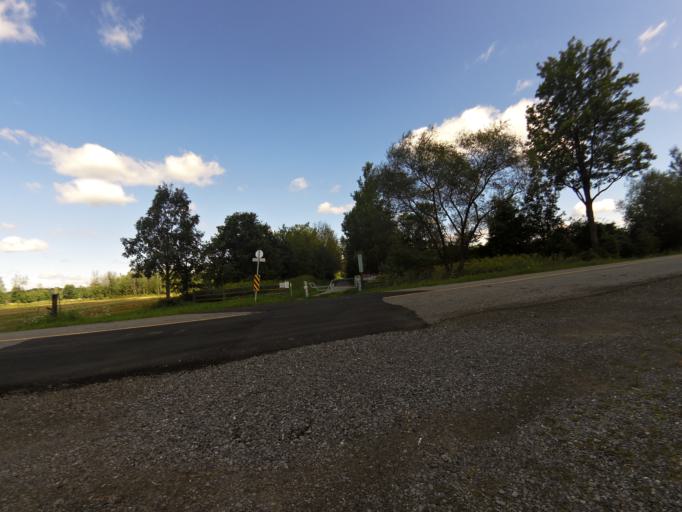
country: CA
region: Ontario
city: Ottawa
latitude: 45.1734
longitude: -75.6177
